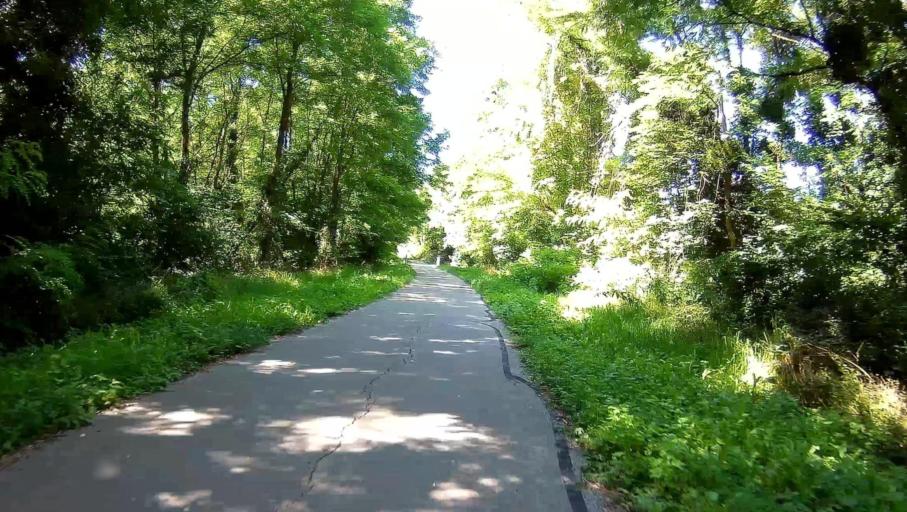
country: FR
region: Bourgogne
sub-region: Departement de Saone-et-Loire
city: Rully
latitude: 46.9046
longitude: 4.6842
